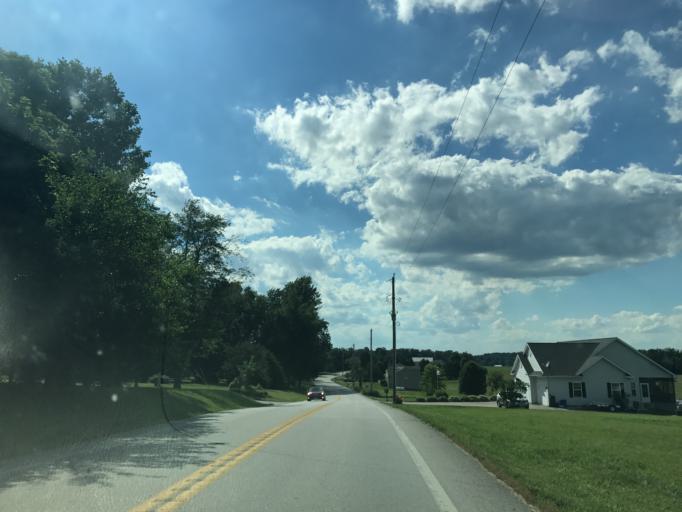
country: US
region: Pennsylvania
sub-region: York County
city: New Freedom
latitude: 39.7298
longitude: -76.7692
